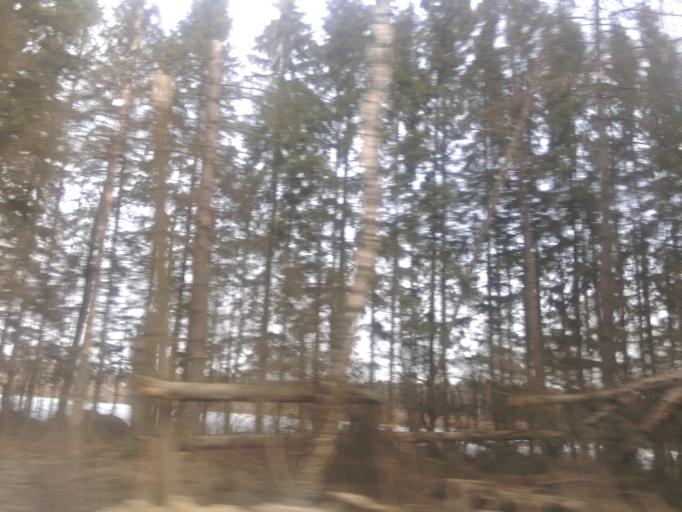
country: RU
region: Moskovskaya
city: Chupryakovo
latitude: 55.5614
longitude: 36.5914
